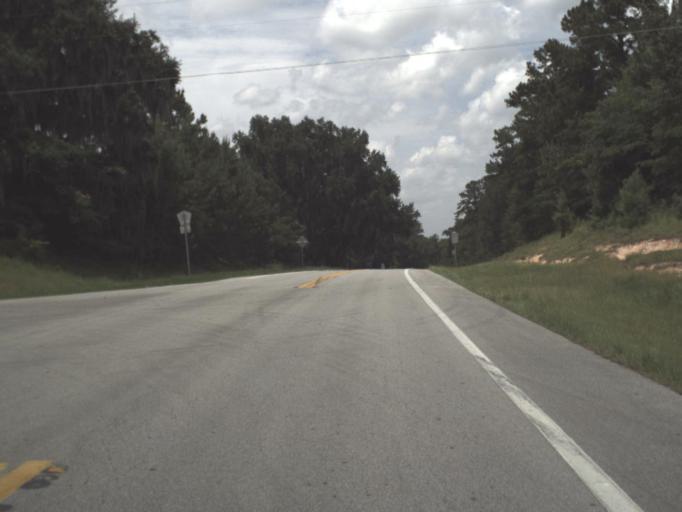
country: US
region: Florida
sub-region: Madison County
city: Madison
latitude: 30.6102
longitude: -83.4354
